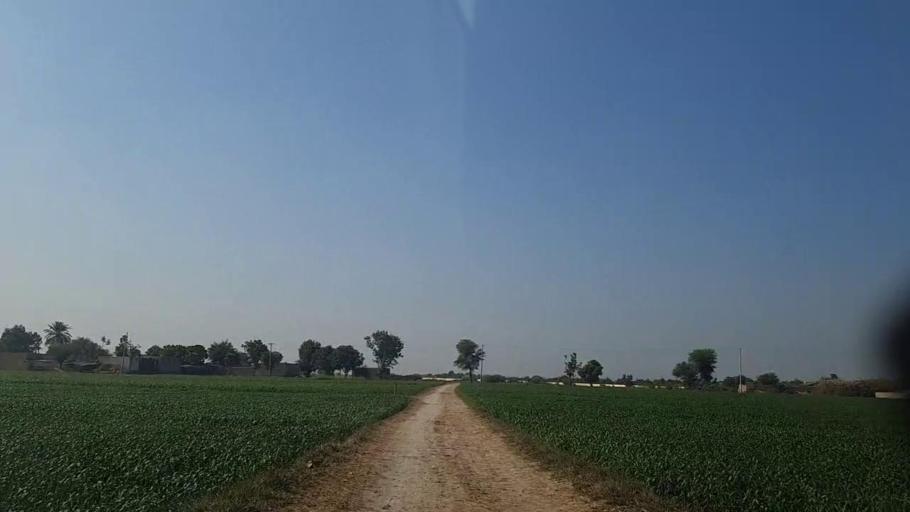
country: PK
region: Sindh
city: Sakrand
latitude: 26.1625
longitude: 68.3225
